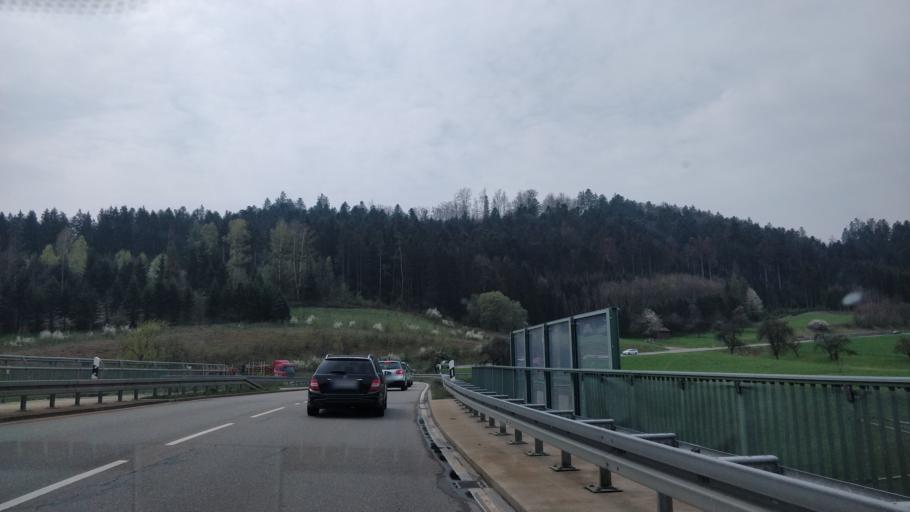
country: DE
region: Baden-Wuerttemberg
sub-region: Regierungsbezirk Stuttgart
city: Fichtenberg
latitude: 48.9876
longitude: 9.6953
